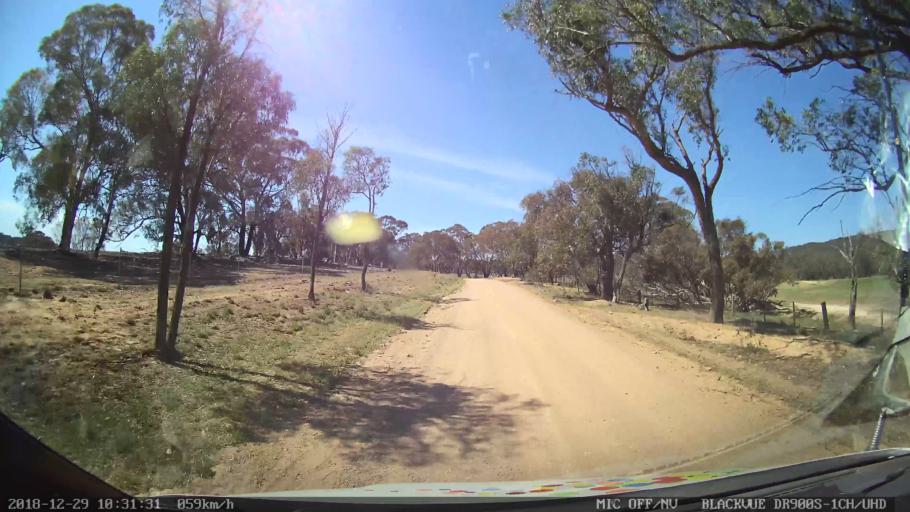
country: AU
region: New South Wales
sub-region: Yass Valley
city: Gundaroo
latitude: -34.9690
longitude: 149.4583
